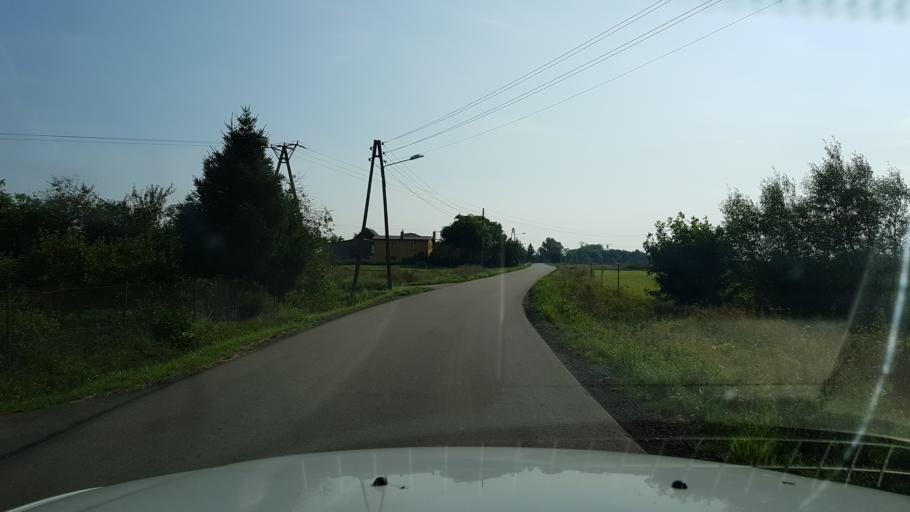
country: PL
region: West Pomeranian Voivodeship
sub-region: Powiat slawienski
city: Slawno
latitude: 54.3744
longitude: 16.5896
